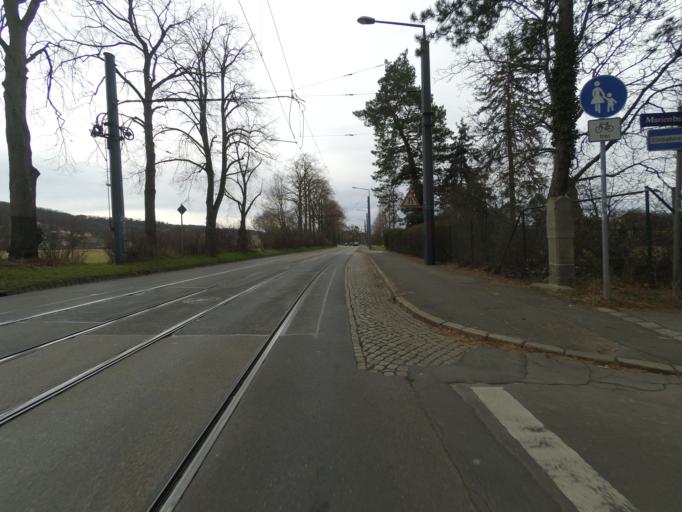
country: DE
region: Saxony
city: Heidenau
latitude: 51.0331
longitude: 13.8267
